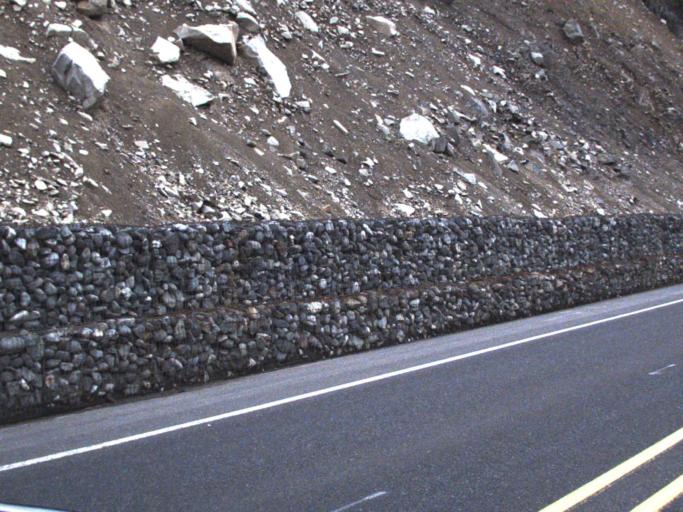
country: US
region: Washington
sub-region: Yakima County
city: Tieton
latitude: 46.6617
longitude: -121.4797
